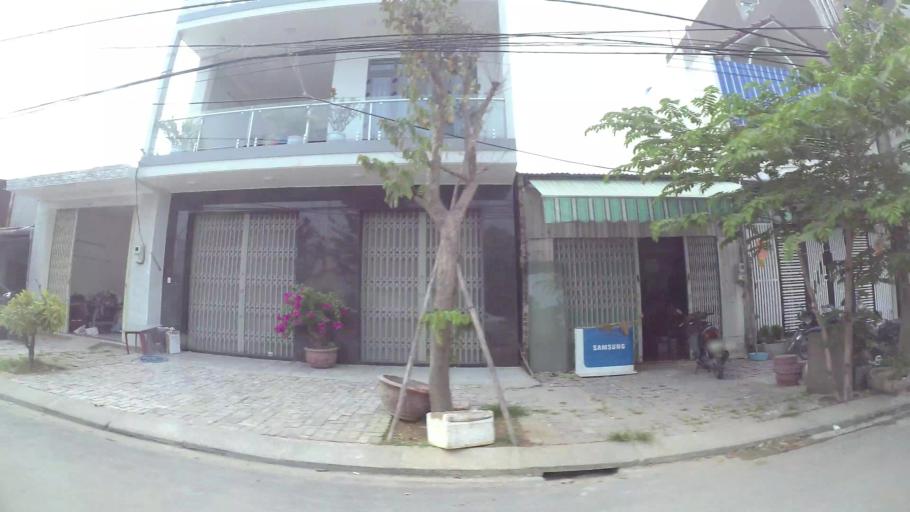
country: VN
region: Da Nang
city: Son Tra
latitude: 16.0890
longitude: 108.2443
